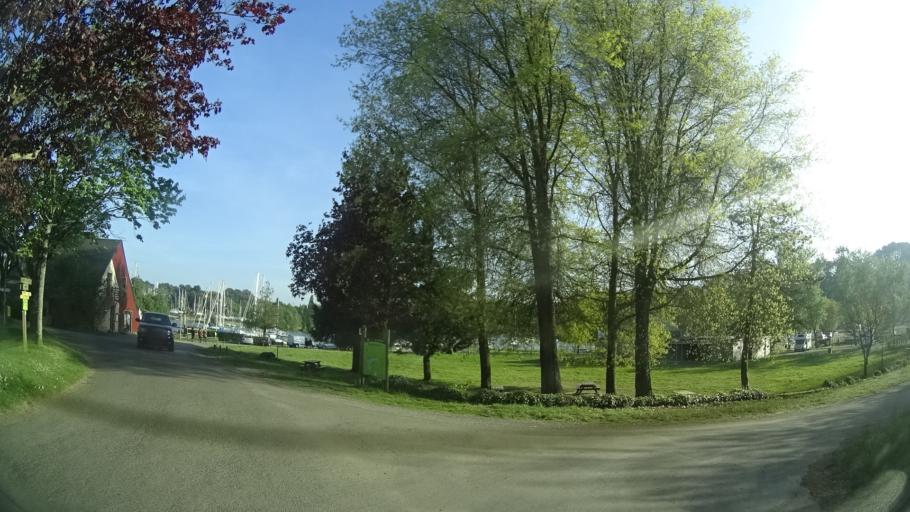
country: FR
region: Brittany
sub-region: Departement du Morbihan
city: Nivillac
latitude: 47.5767
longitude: -2.2839
